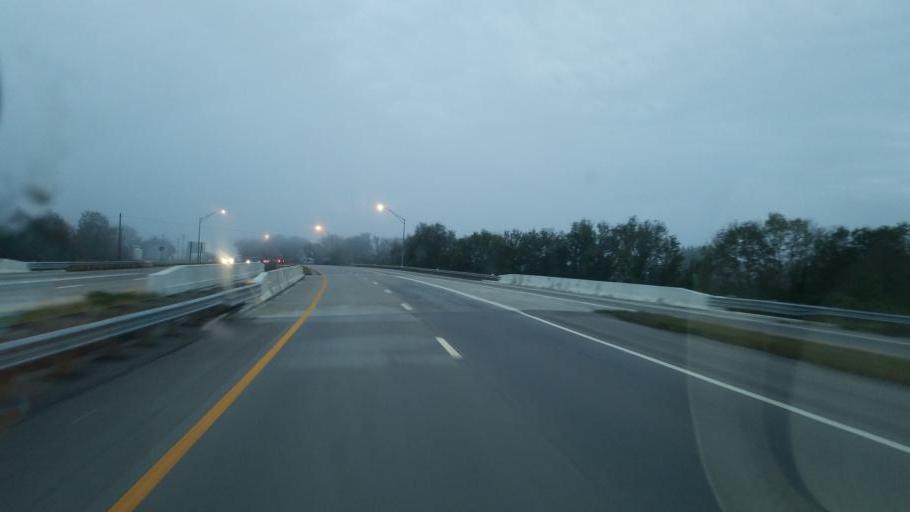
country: US
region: Ohio
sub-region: Pike County
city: Piketon
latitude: 39.0457
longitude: -83.0259
